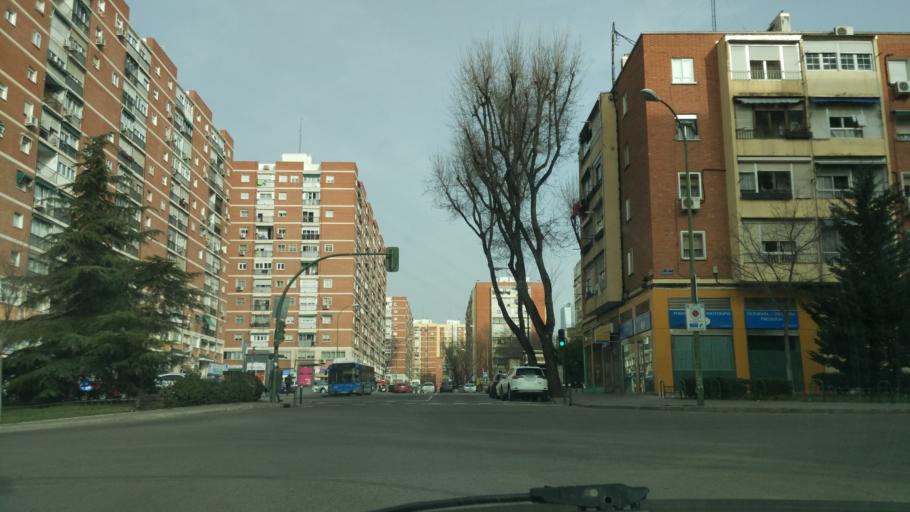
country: ES
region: Madrid
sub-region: Provincia de Madrid
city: Tetuan de las Victorias
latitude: 40.4758
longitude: -3.7161
